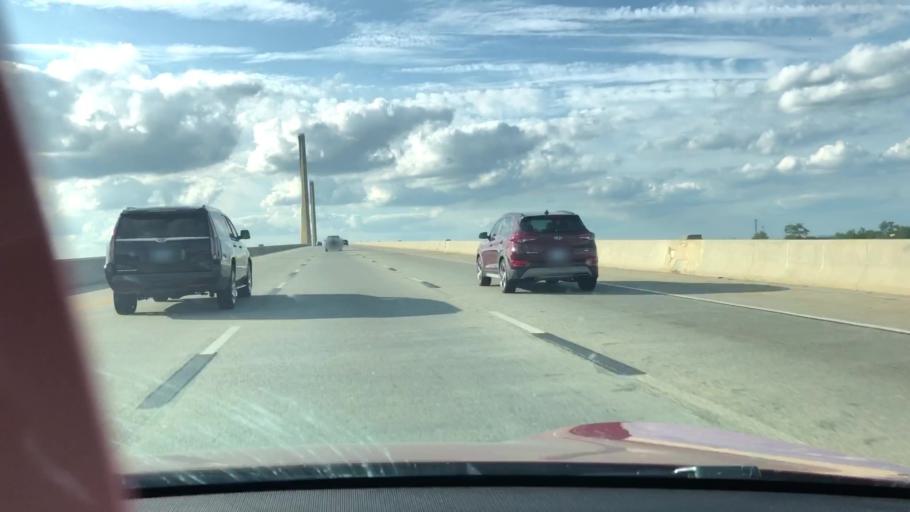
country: US
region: Delaware
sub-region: New Castle County
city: Delaware City
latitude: 39.5460
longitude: -75.6526
